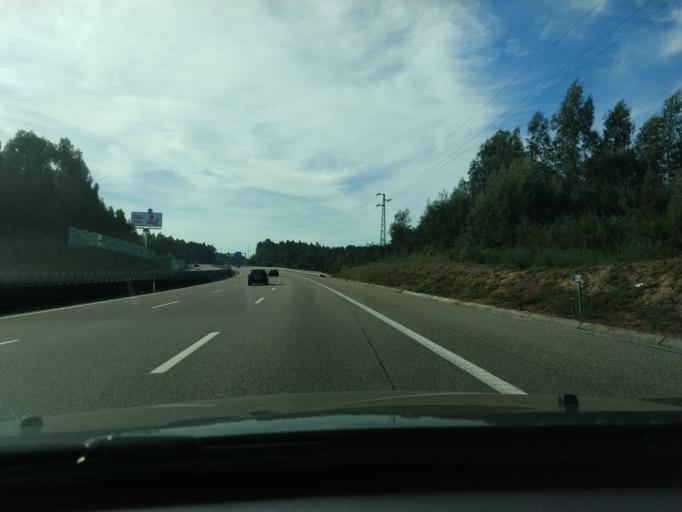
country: PT
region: Aveiro
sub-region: Santa Maria da Feira
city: Rio Meao
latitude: 40.9545
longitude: -8.5724
